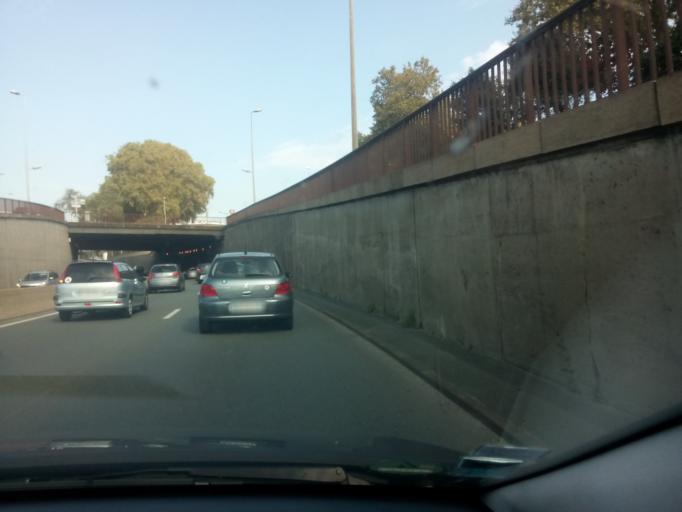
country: FR
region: Pays de la Loire
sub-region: Departement de Maine-et-Loire
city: Angers
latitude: 47.4732
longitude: -0.5570
